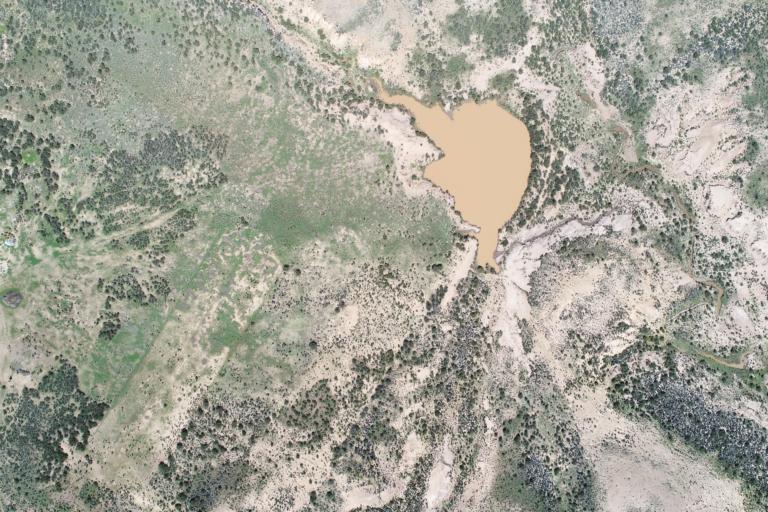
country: BO
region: La Paz
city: Curahuara de Carangas
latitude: -17.2948
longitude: -68.5116
